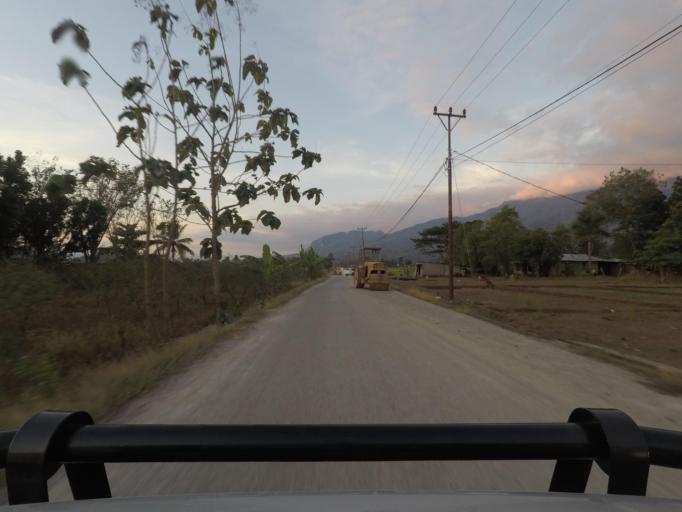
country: TL
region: Bobonaro
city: Maliana
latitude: -8.9872
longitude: 125.2092
